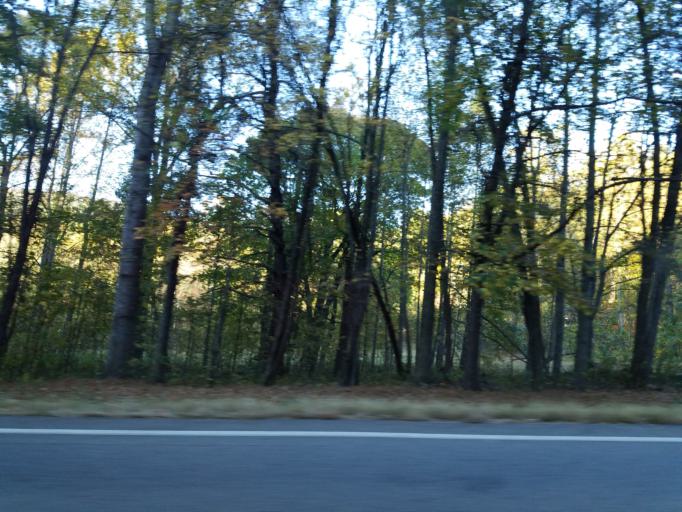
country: US
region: Georgia
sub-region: Dawson County
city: Dawsonville
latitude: 34.5547
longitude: -84.2518
